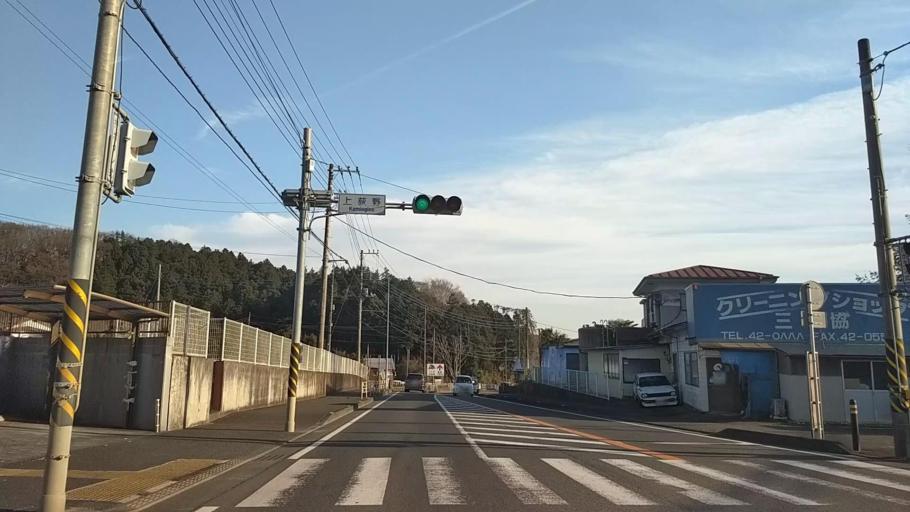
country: JP
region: Kanagawa
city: Zama
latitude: 35.5095
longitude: 139.3048
